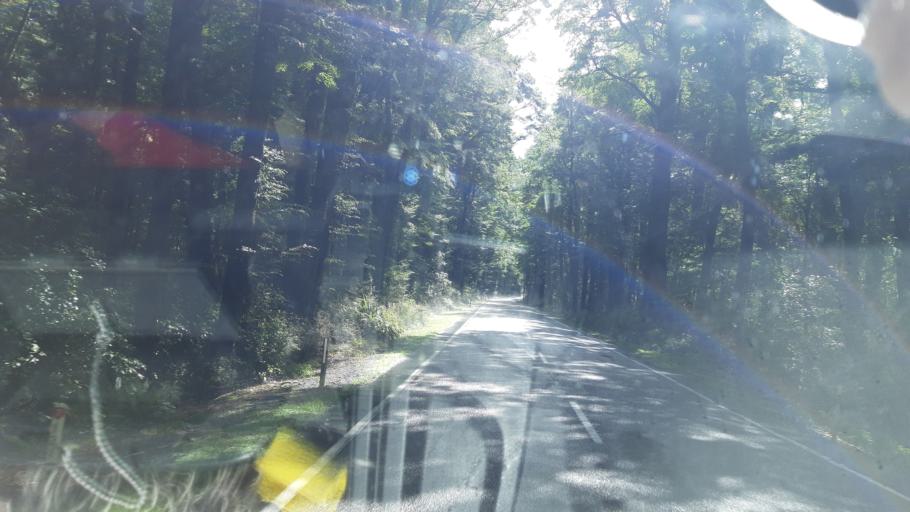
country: NZ
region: Canterbury
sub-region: Hurunui District
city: Amberley
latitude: -42.3775
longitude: 172.2758
